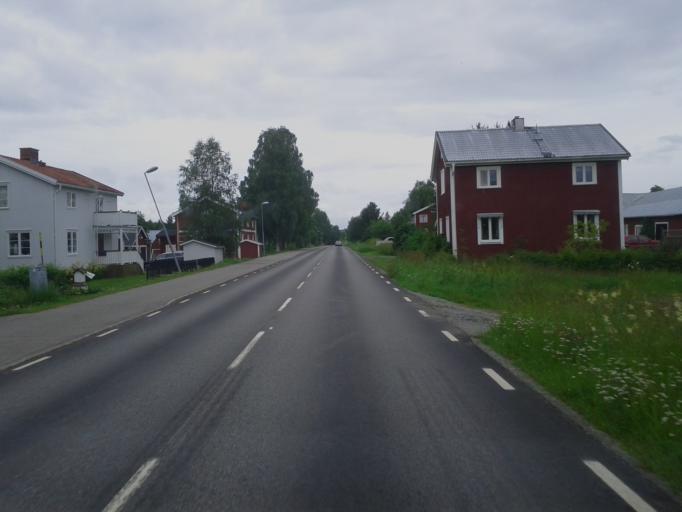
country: SE
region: Vaesterbotten
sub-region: Skelleftea Kommun
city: Viken
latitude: 64.8792
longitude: 20.7905
